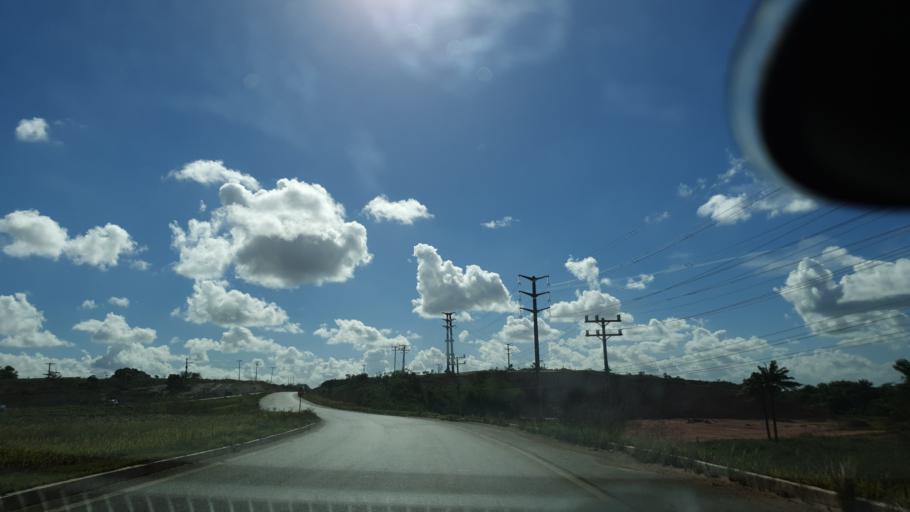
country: BR
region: Bahia
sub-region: Camacari
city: Camacari
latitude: -12.6834
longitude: -38.2486
